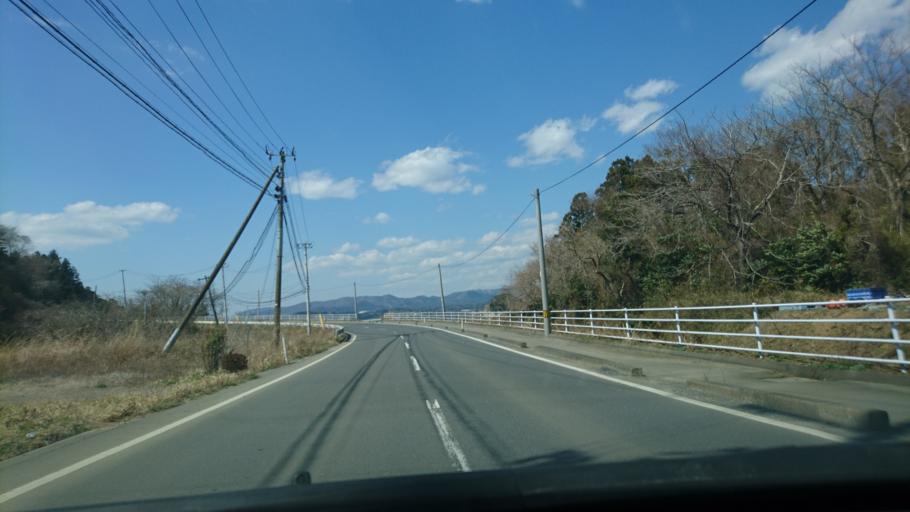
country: JP
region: Miyagi
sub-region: Oshika Gun
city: Onagawa Cho
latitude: 38.6422
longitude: 141.4809
